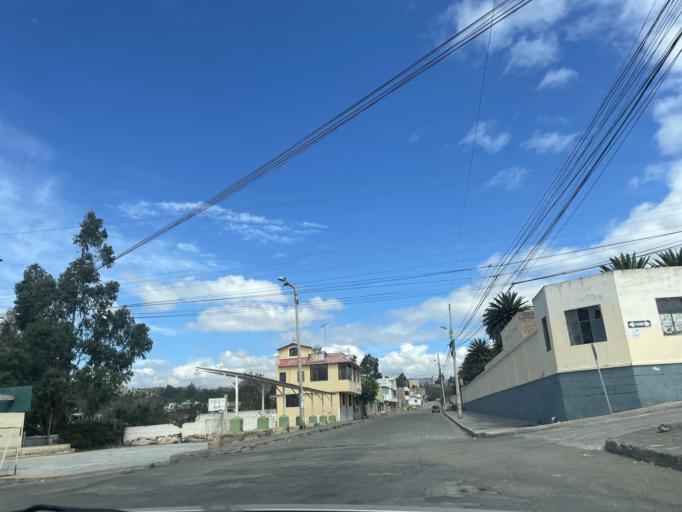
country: EC
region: Chimborazo
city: Guano
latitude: -1.6028
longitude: -78.6448
